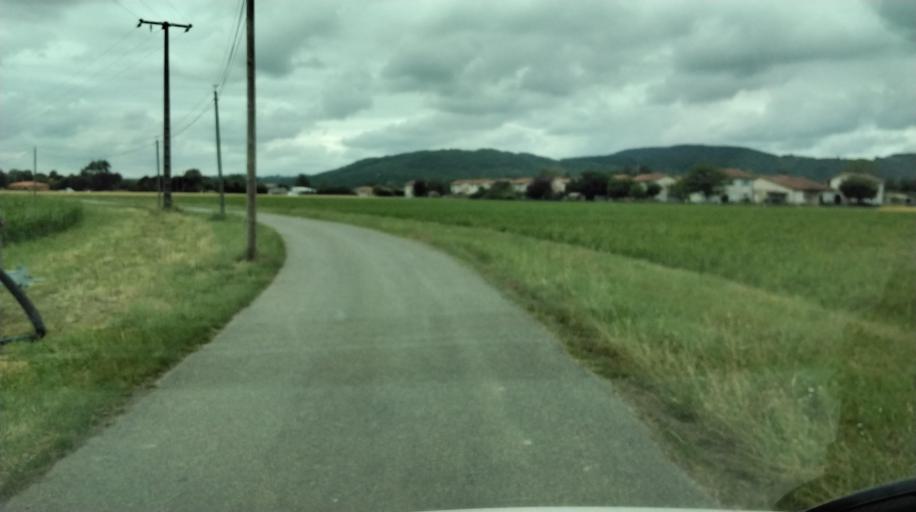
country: FR
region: Midi-Pyrenees
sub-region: Departement de la Haute-Garonne
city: Martres-Tolosane
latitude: 43.2030
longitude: 1.0235
